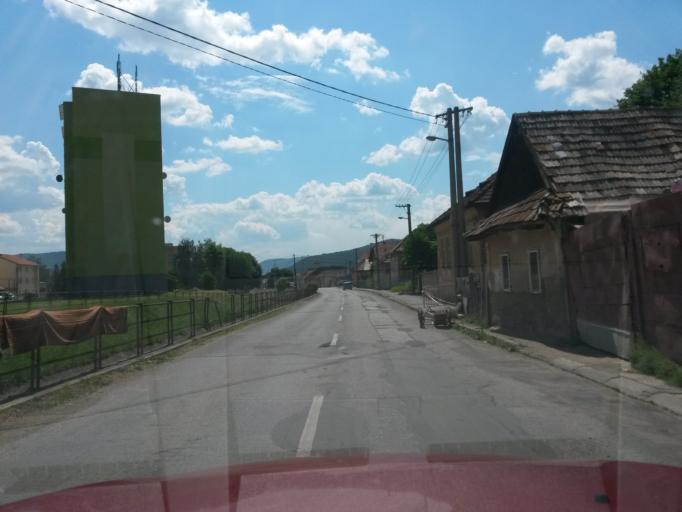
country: SK
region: Kosicky
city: Roznava
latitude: 48.6671
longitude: 20.5395
